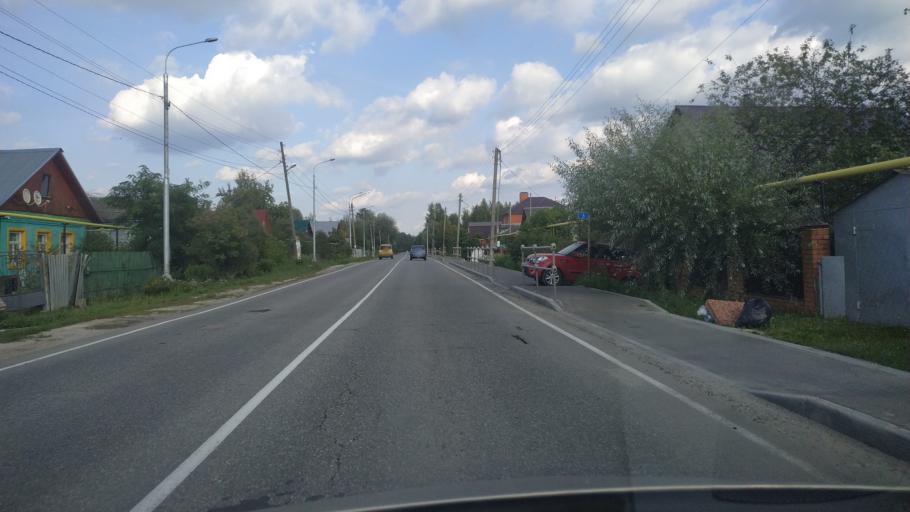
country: RU
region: Moskovskaya
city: Likino-Dulevo
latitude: 55.7296
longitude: 39.0040
